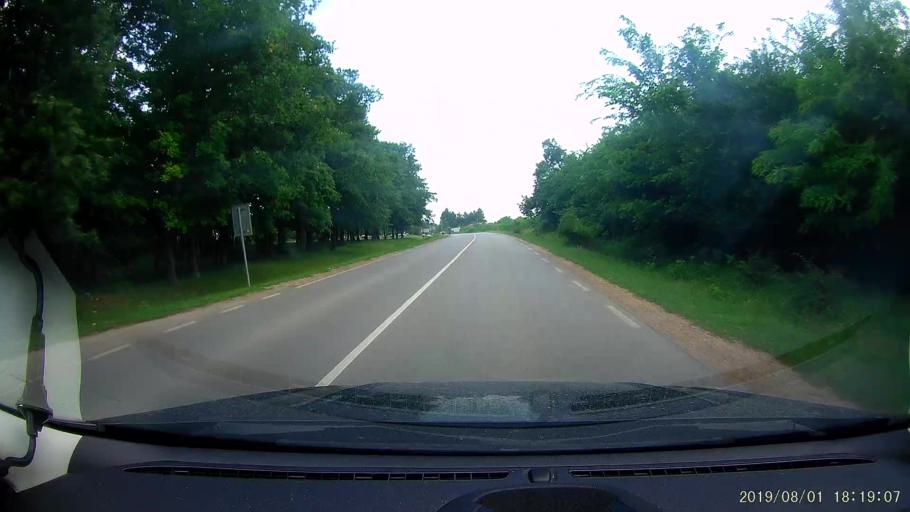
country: BG
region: Shumen
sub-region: Obshtina Kaolinovo
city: Kaolinovo
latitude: 43.6879
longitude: 27.0885
